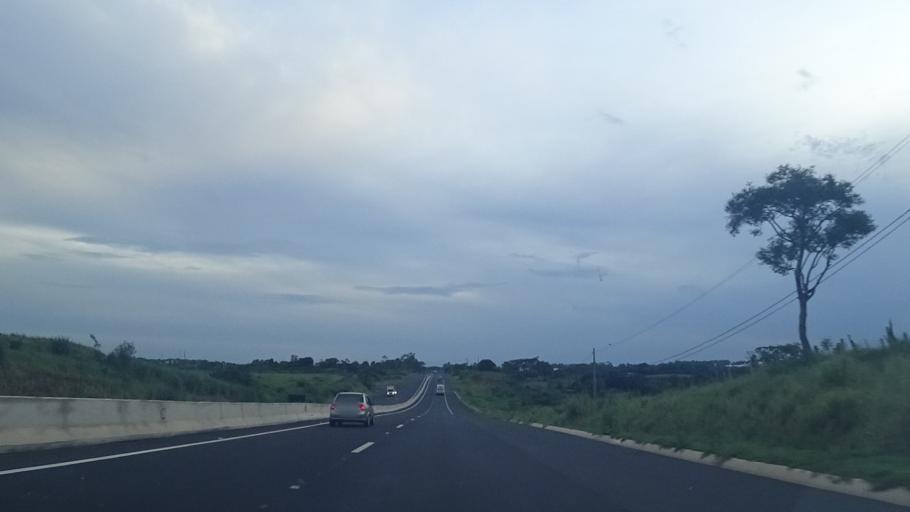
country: BR
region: Sao Paulo
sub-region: Presidente Prudente
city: Presidente Prudente
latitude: -22.1778
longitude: -51.4137
